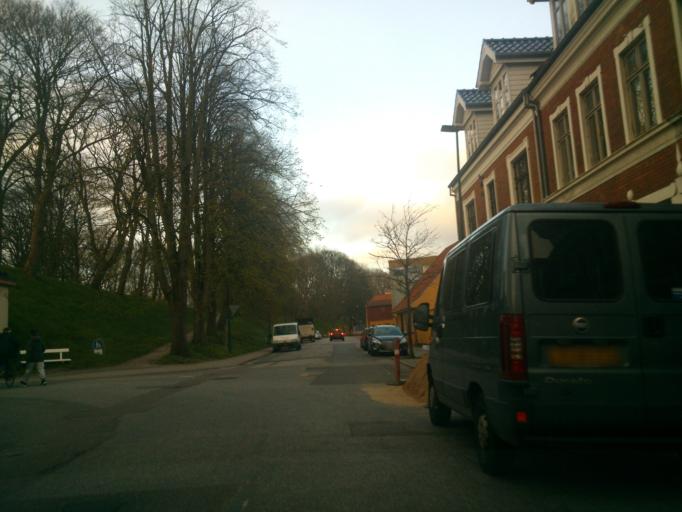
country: DK
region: South Denmark
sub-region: Fredericia Kommune
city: Fredericia
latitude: 55.5696
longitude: 9.7595
